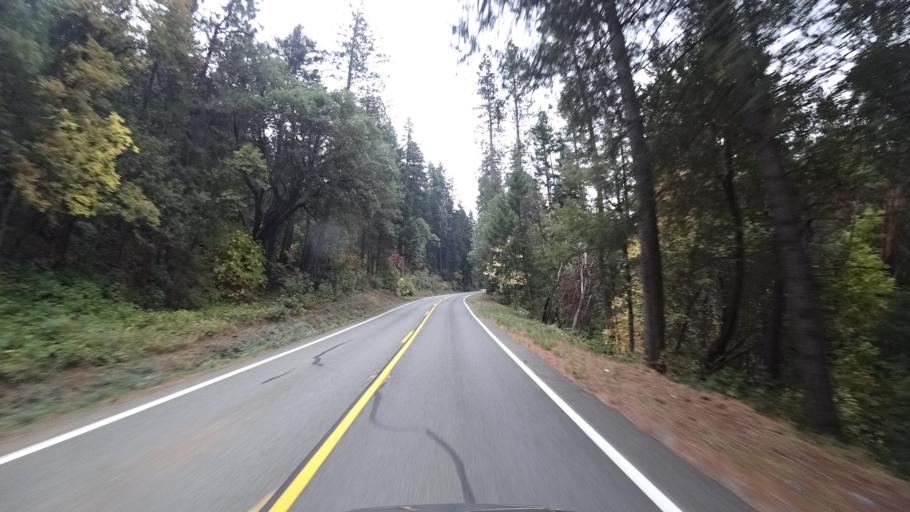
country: US
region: California
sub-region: Siskiyou County
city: Happy Camp
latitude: 41.8015
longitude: -123.3445
